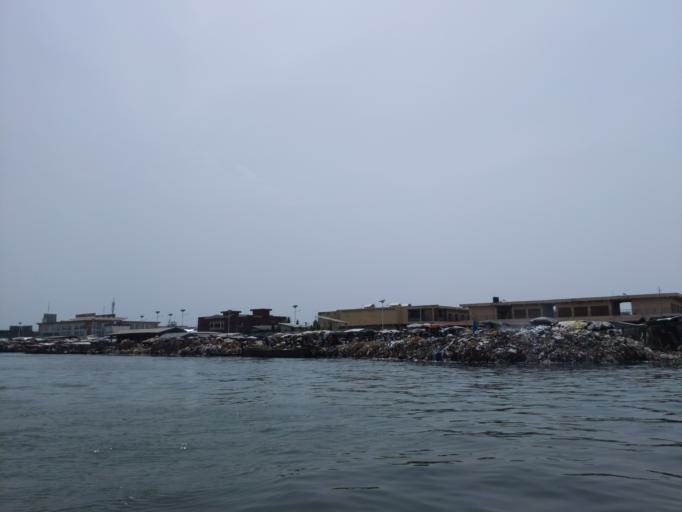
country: BJ
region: Littoral
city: Cotonou
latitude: 6.3752
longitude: 2.4360
